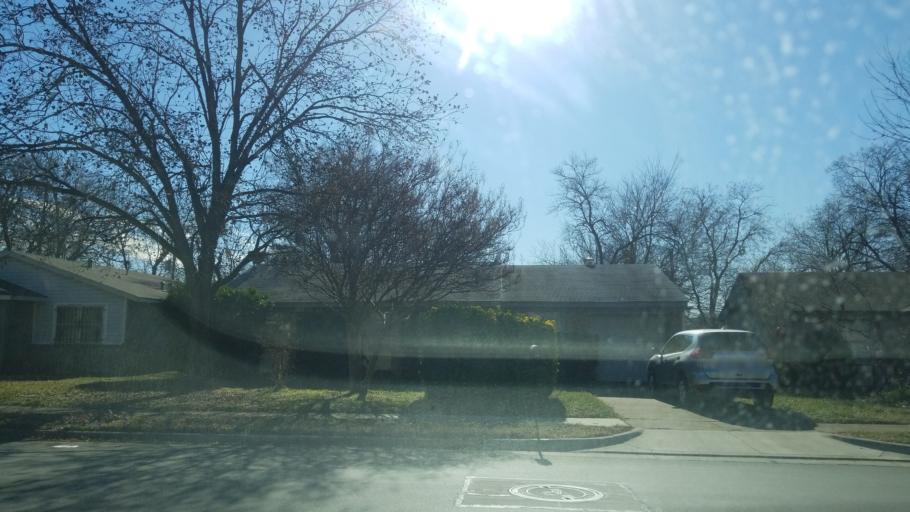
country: US
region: Texas
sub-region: Tarrant County
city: Arlington
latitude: 32.7319
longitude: -97.0600
